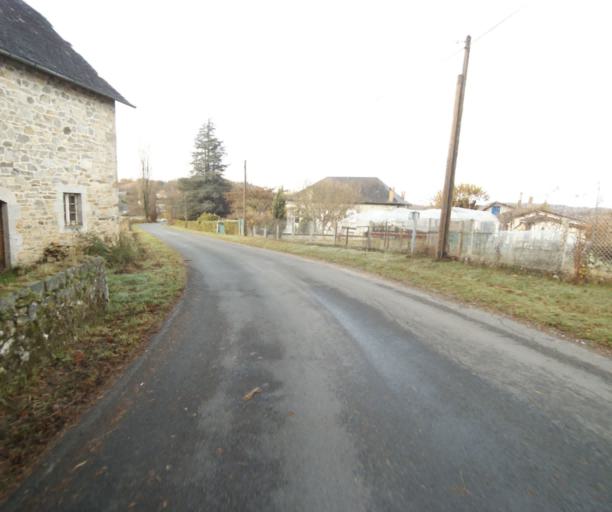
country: FR
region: Limousin
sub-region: Departement de la Correze
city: Cornil
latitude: 45.2120
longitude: 1.7140
